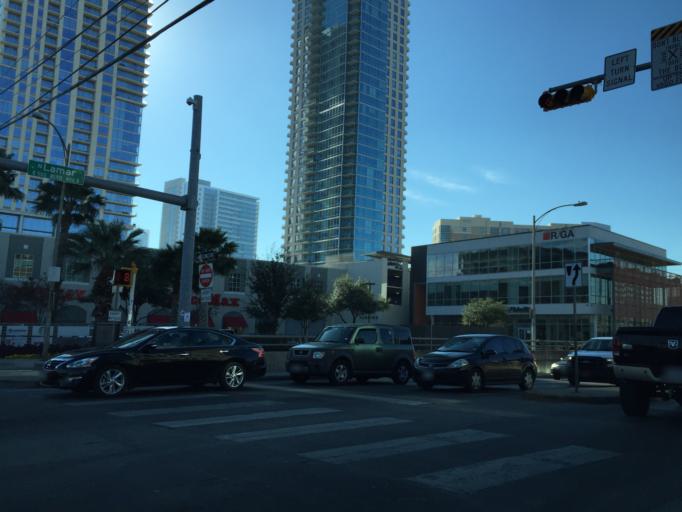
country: US
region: Texas
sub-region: Travis County
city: Austin
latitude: 30.2703
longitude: -97.7548
